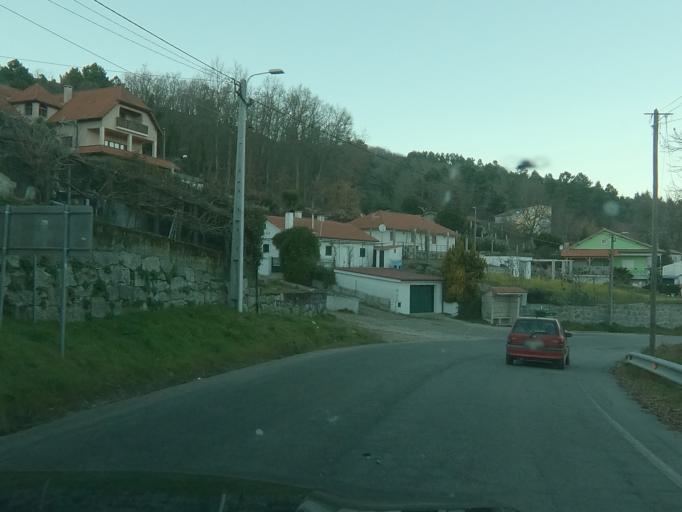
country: PT
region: Vila Real
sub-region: Vila Pouca de Aguiar
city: Vila Pouca de Aguiar
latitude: 41.4943
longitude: -7.6525
